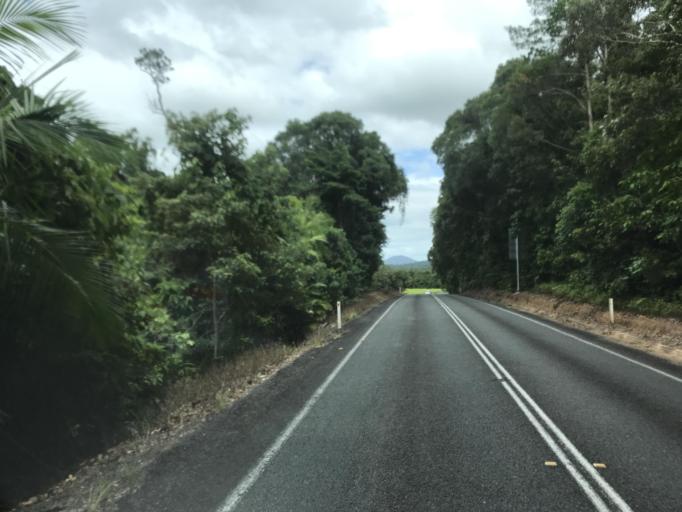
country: AU
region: Queensland
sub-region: Cassowary Coast
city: Innisfail
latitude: -17.8500
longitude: 146.0604
